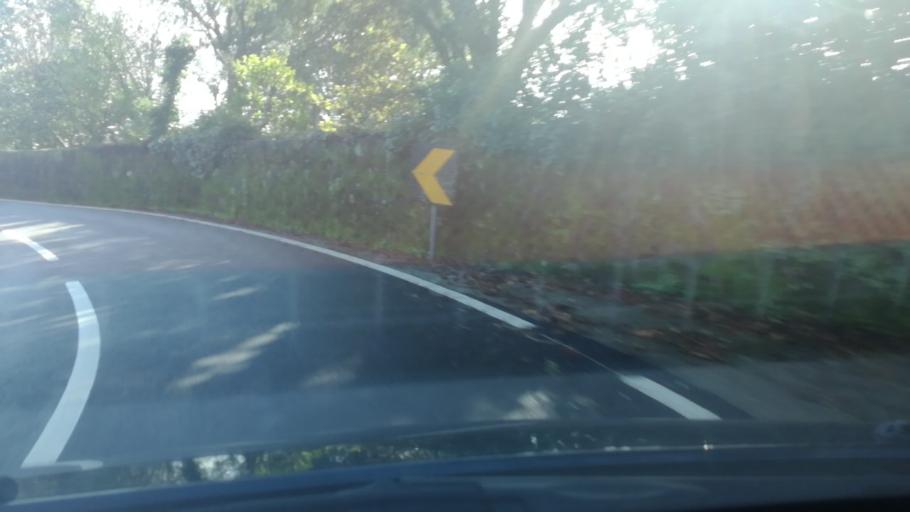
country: PT
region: Braga
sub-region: Guimaraes
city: Ponte
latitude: 41.5277
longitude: -8.3446
